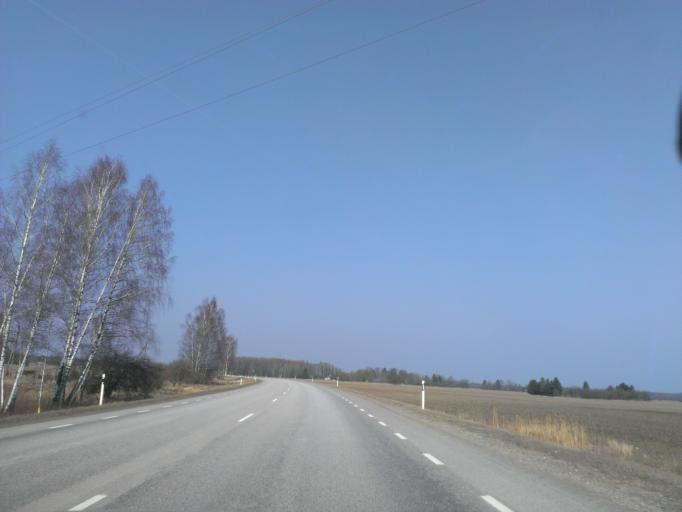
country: EE
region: Saare
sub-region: Orissaare vald
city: Orissaare
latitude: 58.4257
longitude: 22.7899
